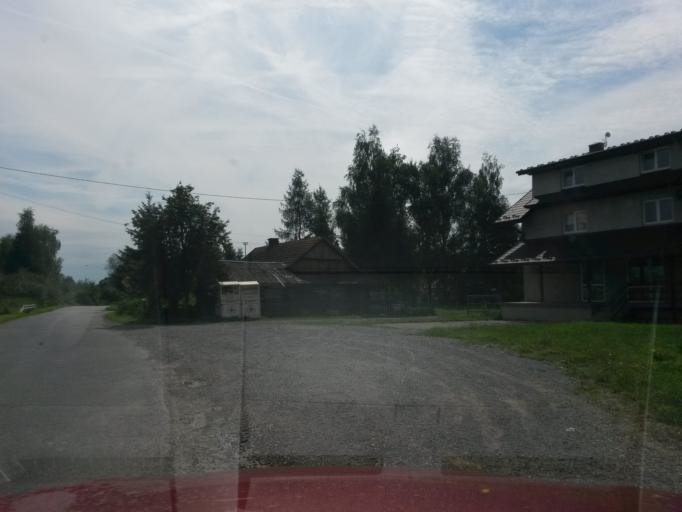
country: PL
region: Lesser Poland Voivodeship
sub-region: Powiat wielicki
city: Szarow
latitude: 49.9880
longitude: 20.2735
